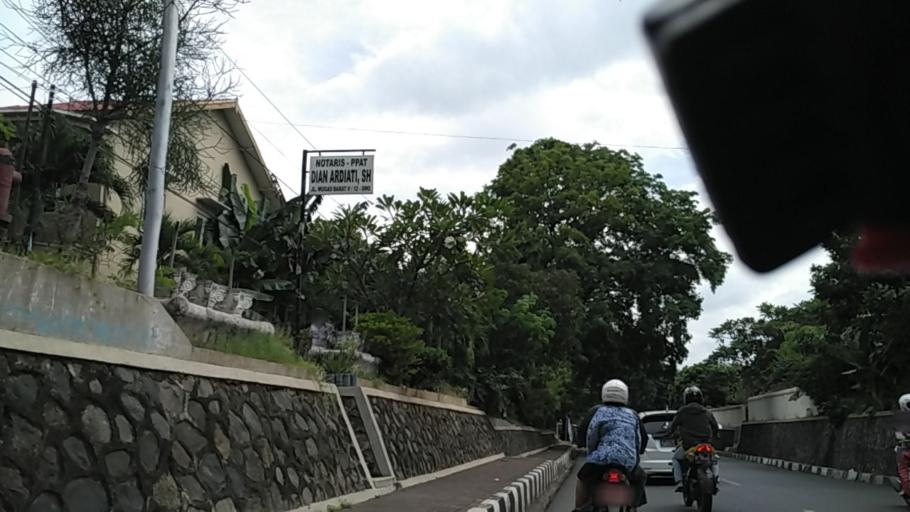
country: ID
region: Central Java
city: Semarang
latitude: -6.9913
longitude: 110.4141
